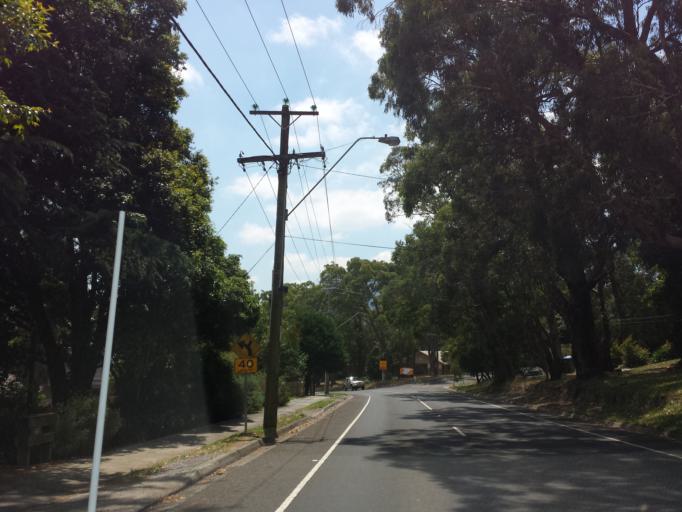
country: AU
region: Victoria
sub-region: Knox
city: The Basin
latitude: -37.8578
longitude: 145.3138
